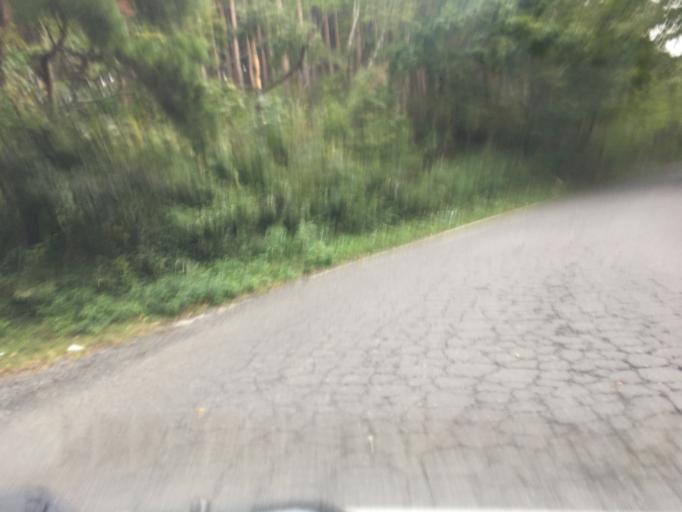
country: JP
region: Miyagi
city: Marumori
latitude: 37.8756
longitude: 140.6982
